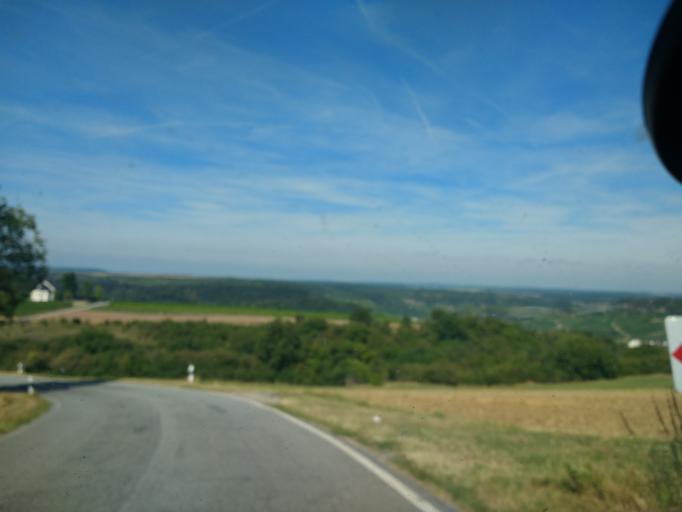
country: DE
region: Rheinland-Pfalz
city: Nittel
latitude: 49.6430
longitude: 6.4569
